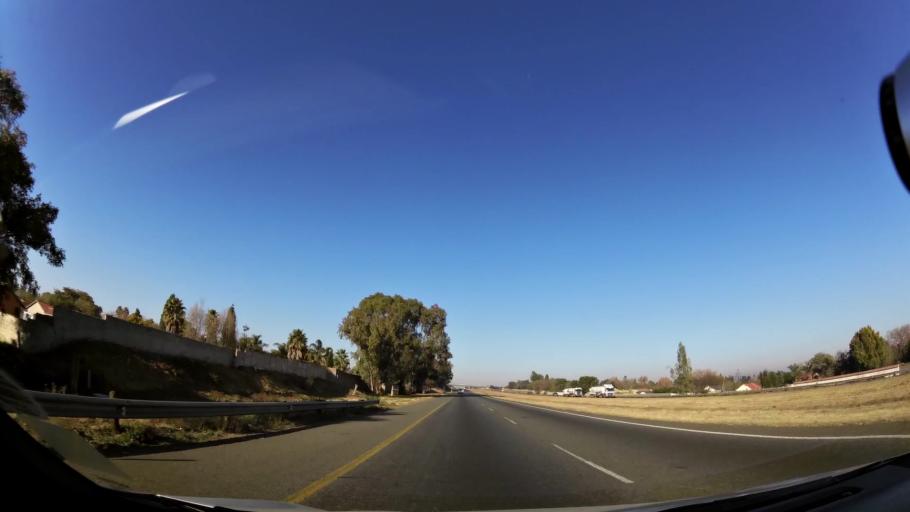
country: ZA
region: Gauteng
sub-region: Ekurhuleni Metropolitan Municipality
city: Germiston
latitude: -26.3422
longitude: 28.1050
